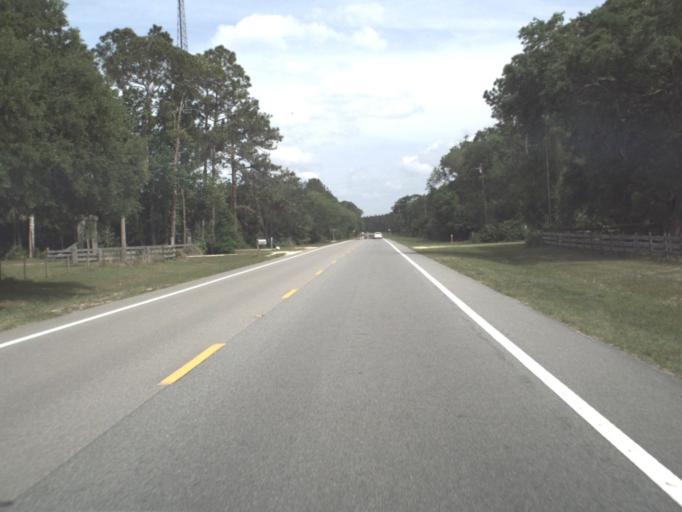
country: US
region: Florida
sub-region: Putnam County
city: Crescent City
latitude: 29.4858
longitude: -81.4618
